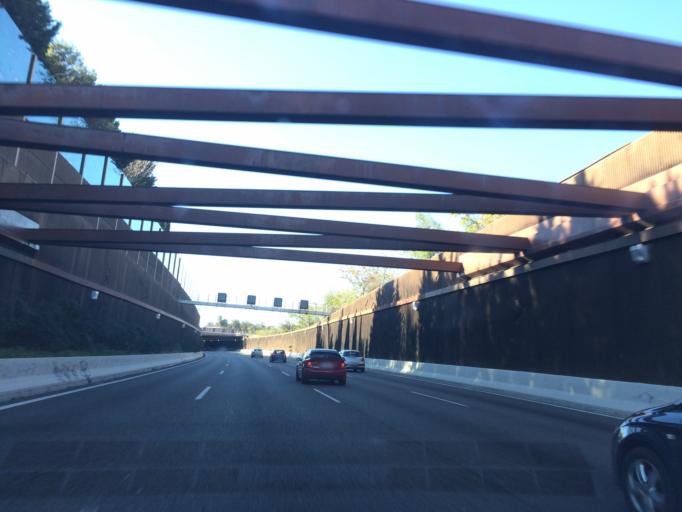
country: ES
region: Madrid
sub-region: Provincia de Madrid
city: El Pardo
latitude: 40.4736
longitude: -3.7665
